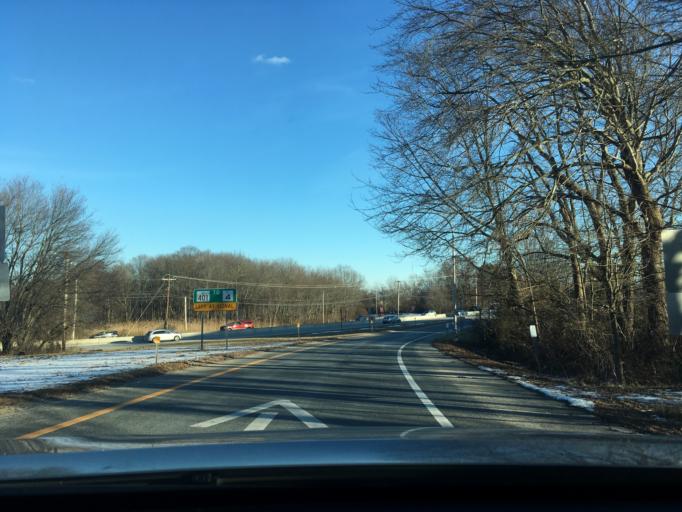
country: US
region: Rhode Island
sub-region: Kent County
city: West Warwick
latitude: 41.6662
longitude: -71.5007
